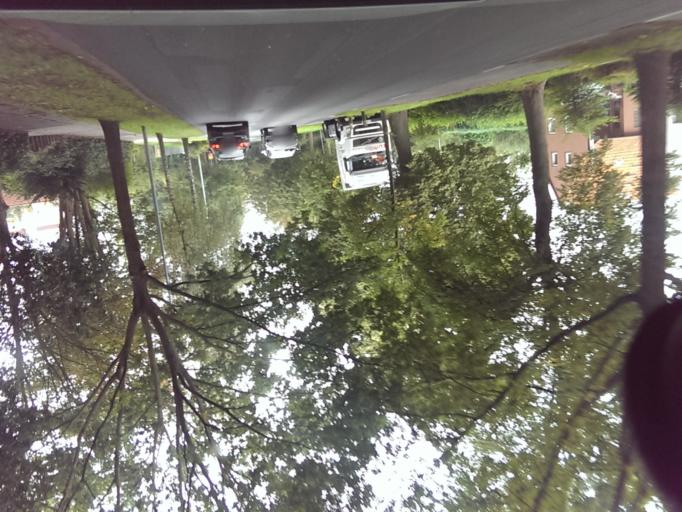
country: DE
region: Lower Saxony
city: Isernhagen Farster Bauerschaft
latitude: 52.4307
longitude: 9.8539
